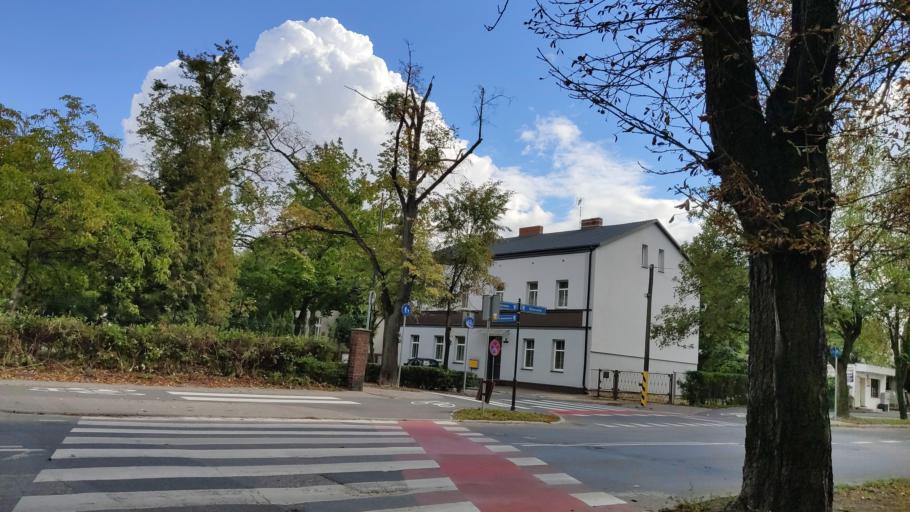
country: PL
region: Kujawsko-Pomorskie
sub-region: Powiat mogilenski
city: Mogilno
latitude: 52.6579
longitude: 17.9466
